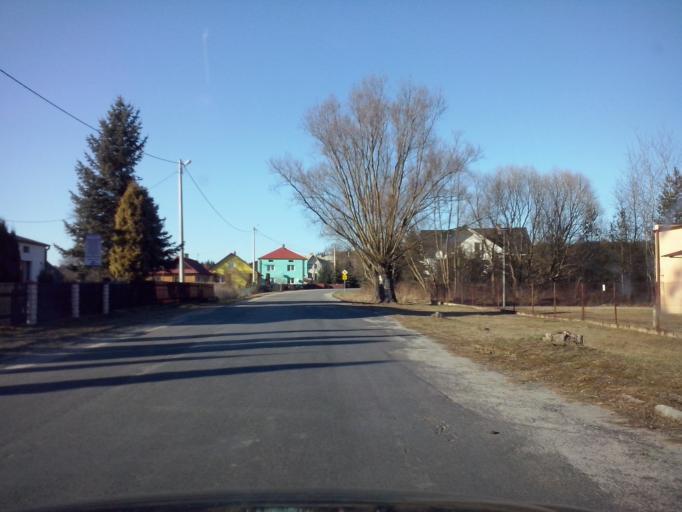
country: PL
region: Subcarpathian Voivodeship
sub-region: Powiat nizanski
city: Harasiuki
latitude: 50.5271
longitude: 22.4501
